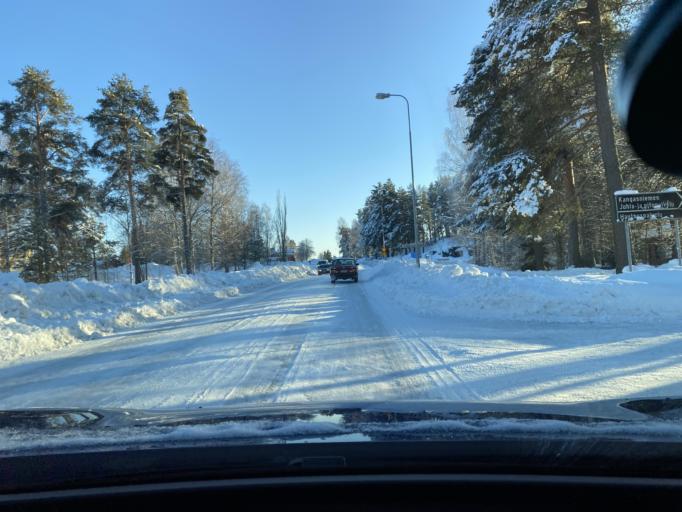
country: FI
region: Southern Savonia
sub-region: Mikkeli
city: Kangasniemi
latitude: 61.9918
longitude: 26.6341
